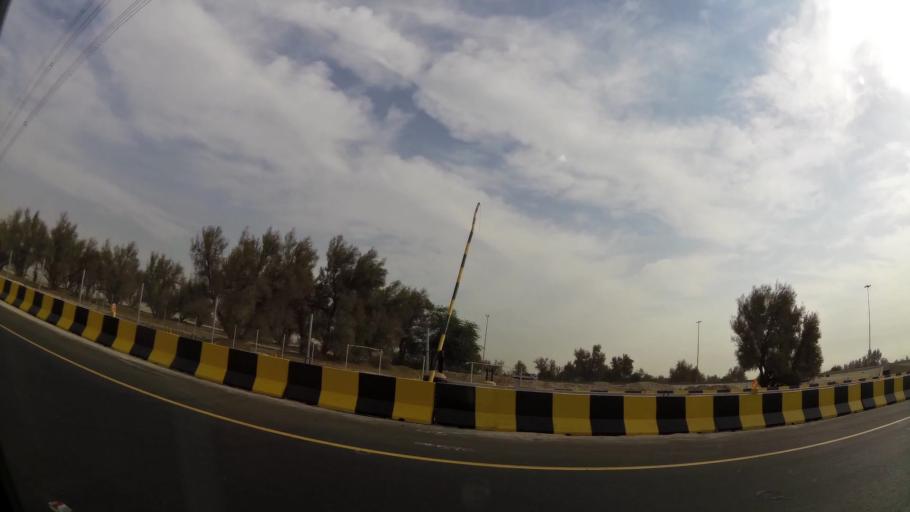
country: KW
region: Muhafazat al Jahra'
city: Al Jahra'
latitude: 29.2856
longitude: 47.7875
